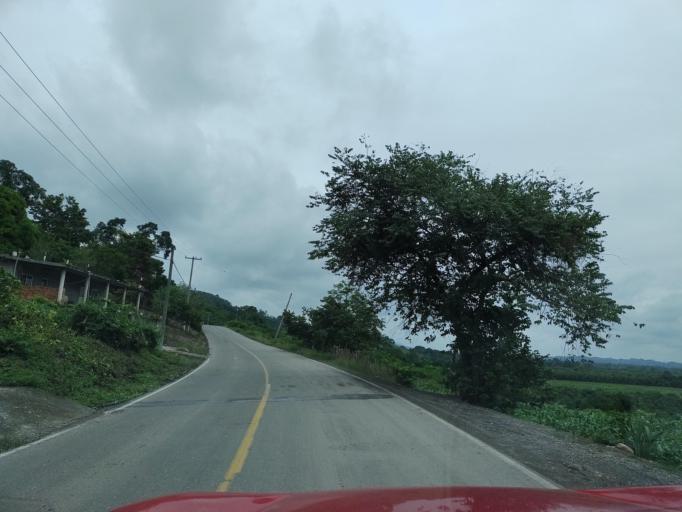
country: MX
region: Puebla
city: Espinal
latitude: 20.2618
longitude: -97.3659
